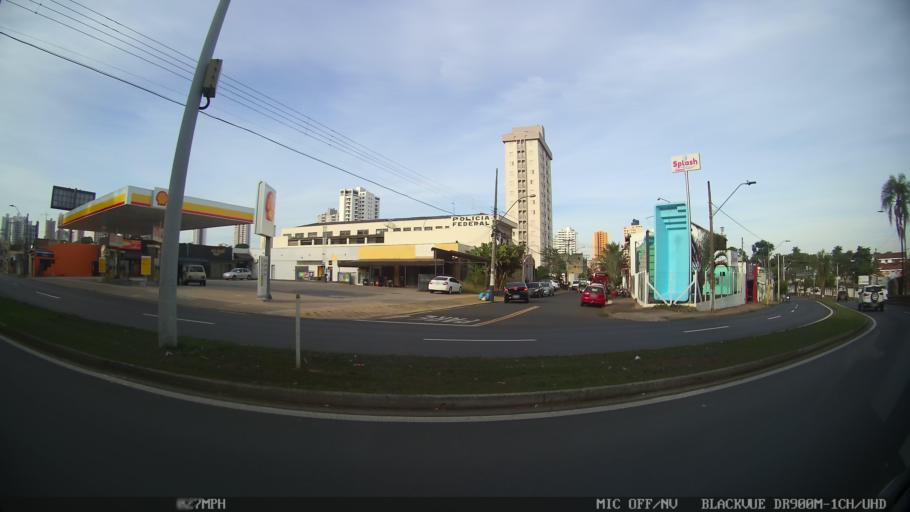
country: BR
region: Sao Paulo
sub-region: Piracicaba
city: Piracicaba
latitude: -22.7084
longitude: -47.6443
